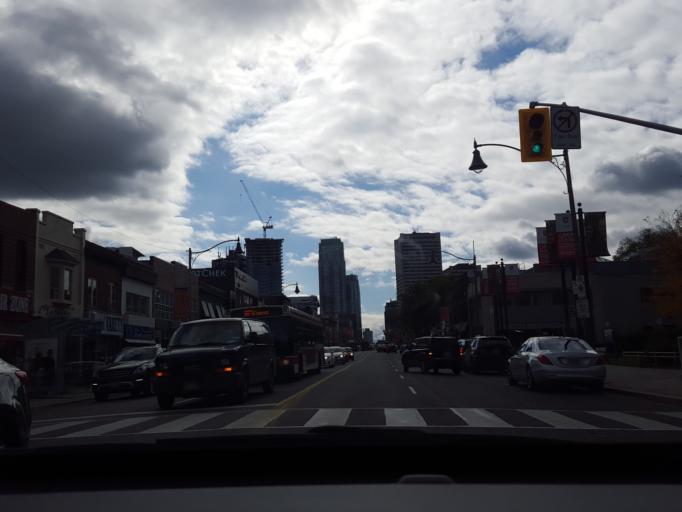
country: CA
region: Ontario
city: Toronto
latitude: 43.7136
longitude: -79.3998
